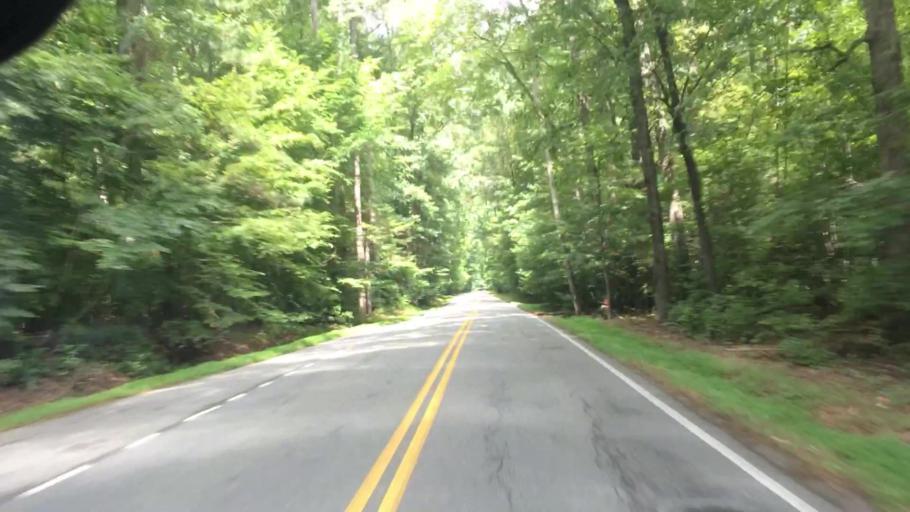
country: US
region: Virginia
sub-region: James City County
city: Williamsburg
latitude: 37.2488
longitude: -76.7978
